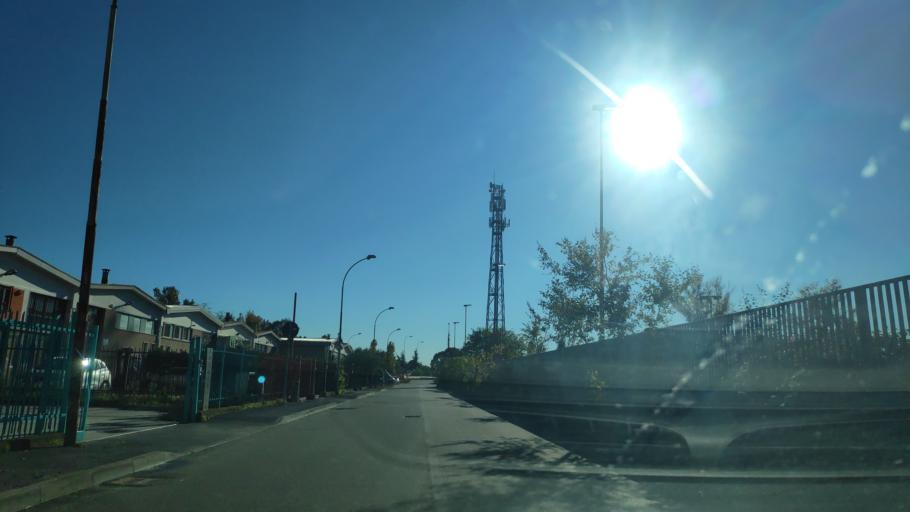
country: IT
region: Lombardy
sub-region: Citta metropolitana di Milano
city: Fizzonasco
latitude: 45.3717
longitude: 9.1761
